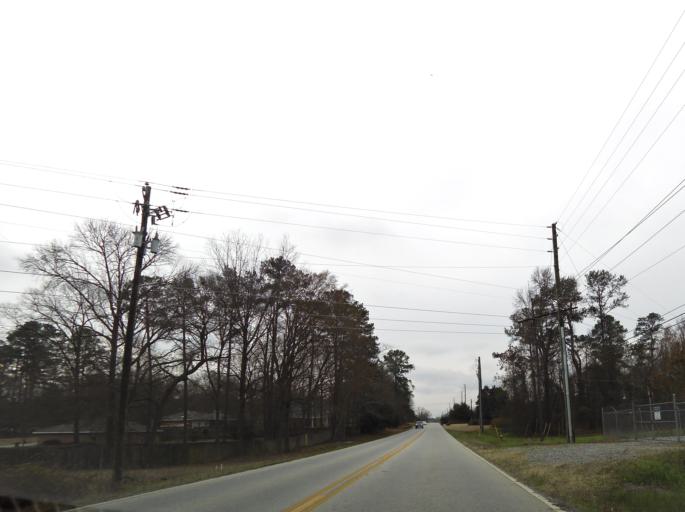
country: US
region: Georgia
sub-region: Houston County
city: Robins Air Force Base
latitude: 32.5662
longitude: -83.5877
